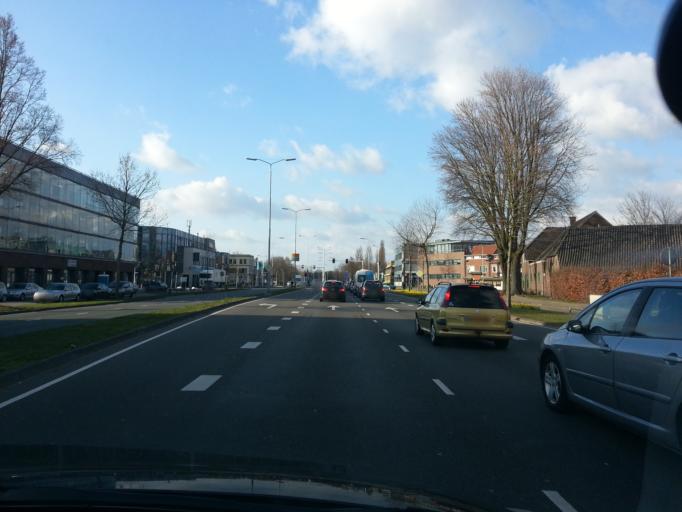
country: NL
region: North Brabant
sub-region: Gemeente Eindhoven
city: Lakerlopen
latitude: 51.4402
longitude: 5.5045
